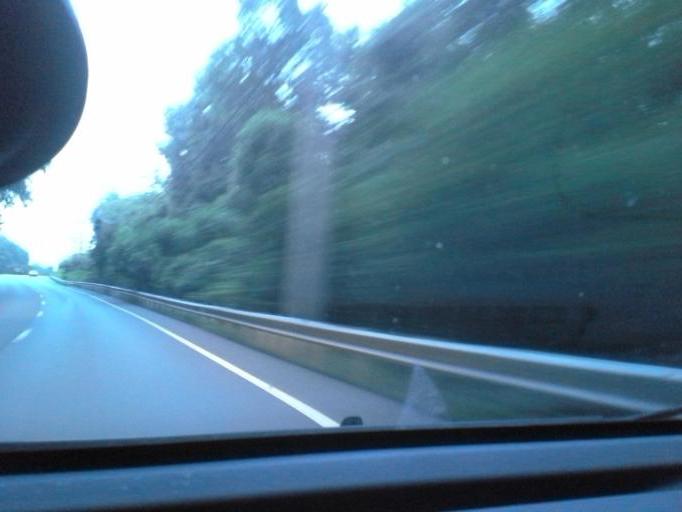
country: US
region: Maryland
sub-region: Calvert County
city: Chesapeake Beach
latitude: 38.6993
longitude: -76.5560
